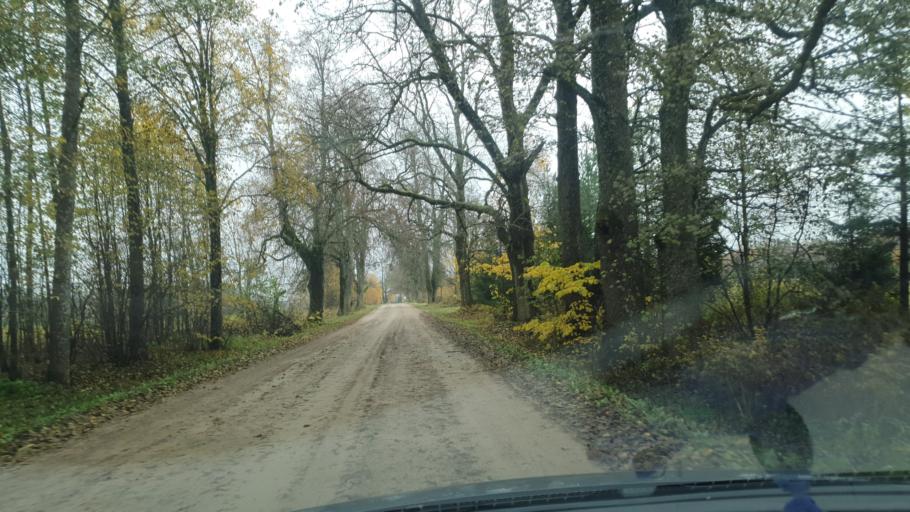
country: EE
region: Viljandimaa
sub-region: Karksi vald
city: Karksi-Nuia
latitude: 57.9991
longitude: 25.6627
